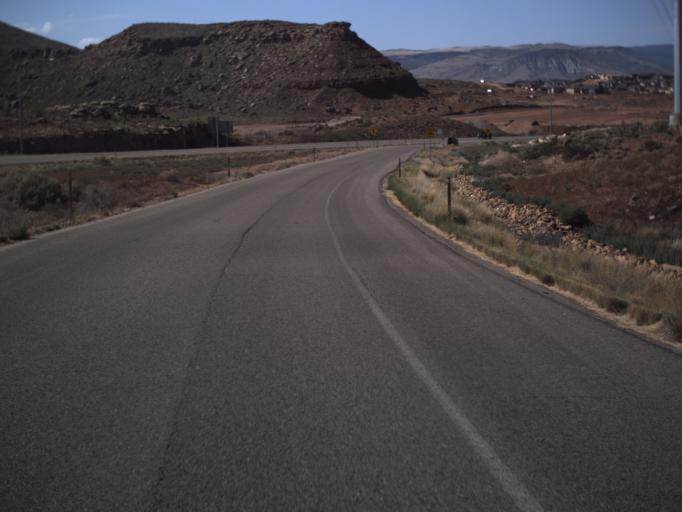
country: US
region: Utah
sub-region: Washington County
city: Washington
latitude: 37.0133
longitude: -113.4968
